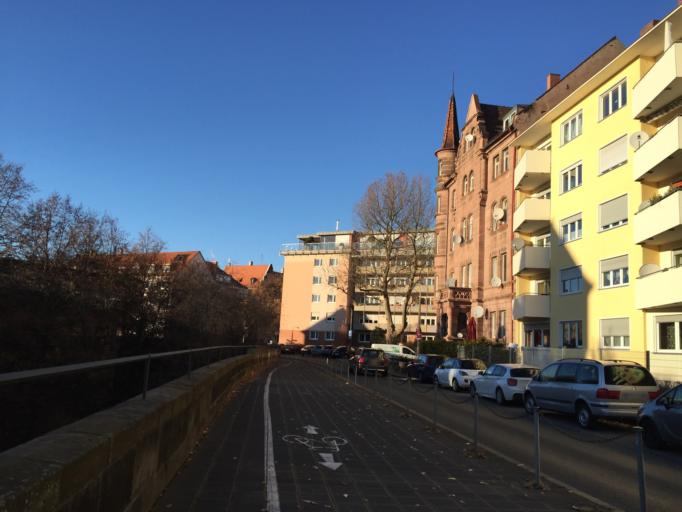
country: DE
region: Bavaria
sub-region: Regierungsbezirk Mittelfranken
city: Nuernberg
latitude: 49.4592
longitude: 11.0868
